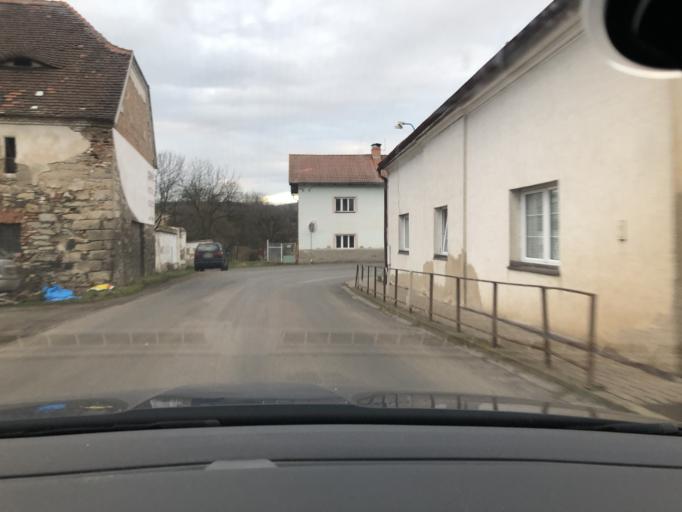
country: CZ
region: Ustecky
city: Rehlovice
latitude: 50.6073
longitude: 13.9503
